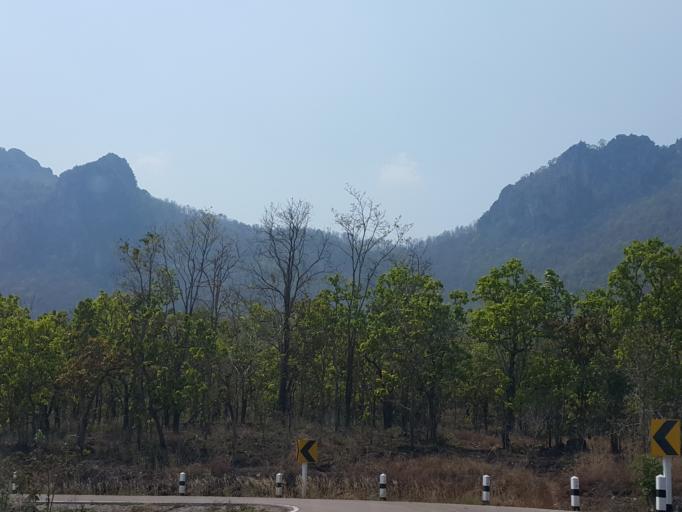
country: TH
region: Lampang
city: Chae Hom
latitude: 18.7461
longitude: 99.5458
